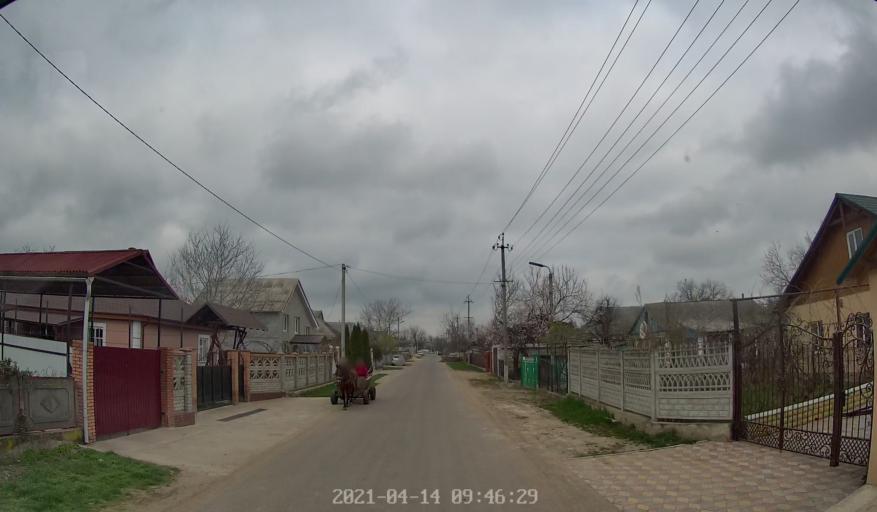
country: MD
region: Chisinau
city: Vadul lui Voda
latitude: 47.1350
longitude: 29.1222
